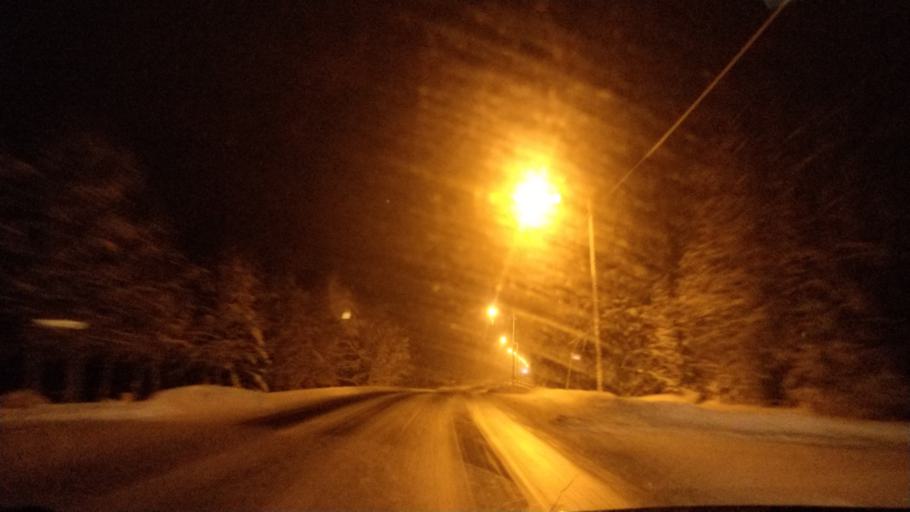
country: FI
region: Lapland
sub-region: Rovaniemi
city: Rovaniemi
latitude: 66.4151
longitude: 25.4115
